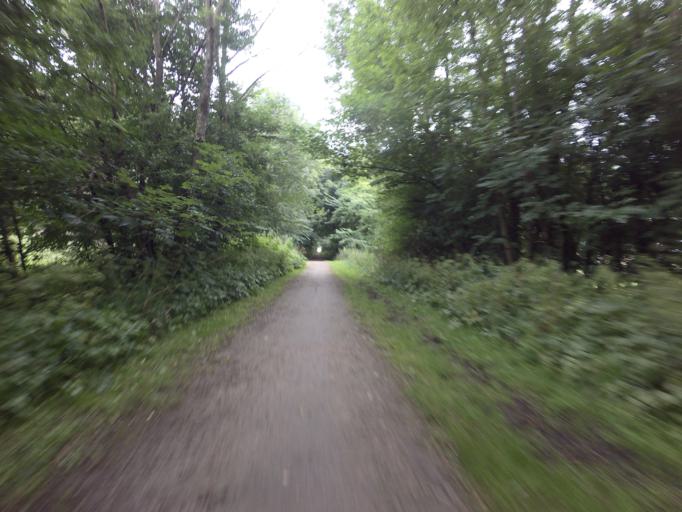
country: DK
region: North Denmark
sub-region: Alborg Kommune
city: Vadum
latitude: 57.1156
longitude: 9.8752
